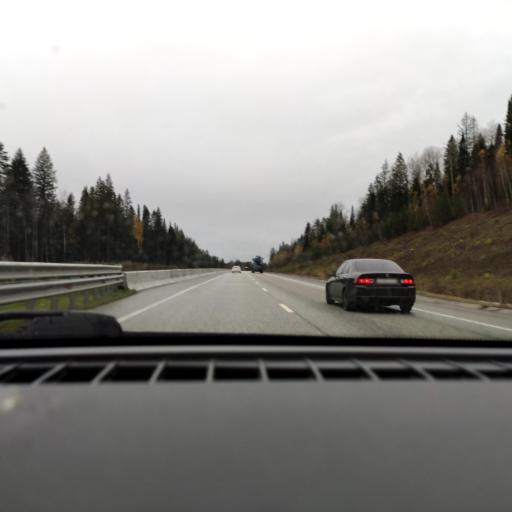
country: RU
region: Perm
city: Ferma
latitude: 57.9807
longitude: 56.3933
